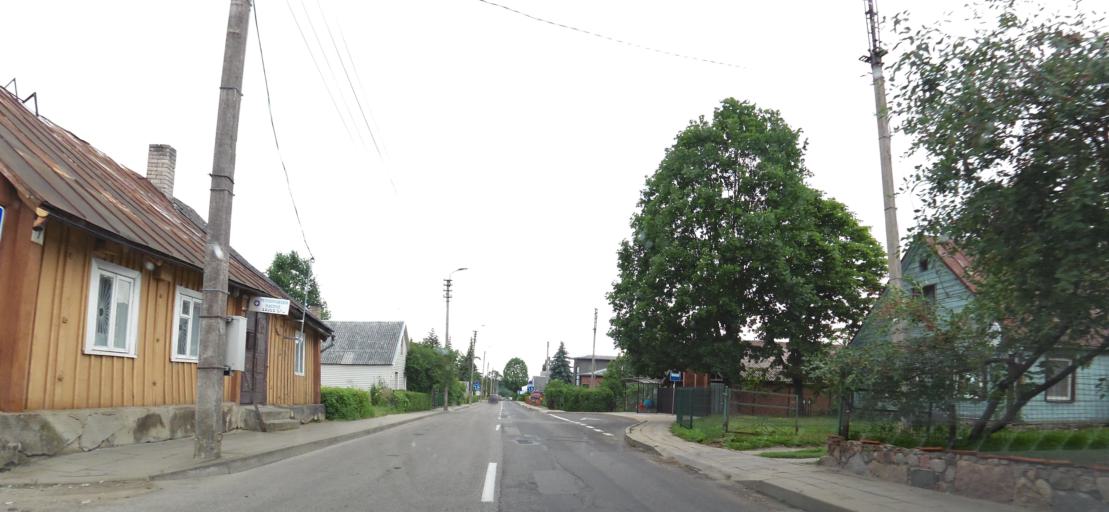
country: LT
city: Kupiskis
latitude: 55.8406
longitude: 24.9749
